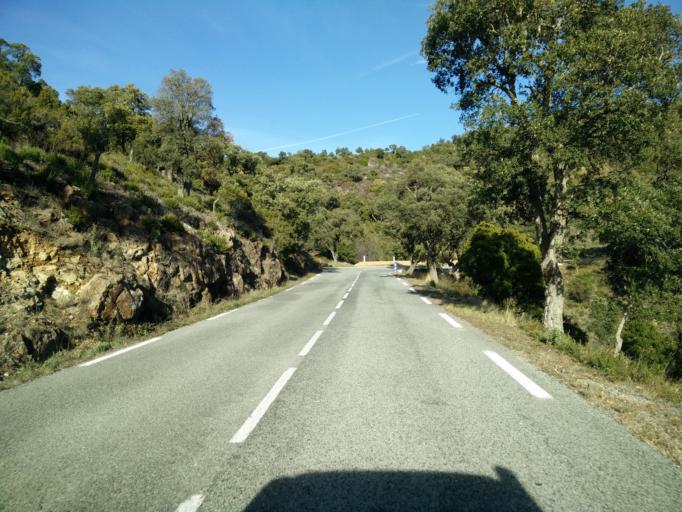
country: FR
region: Provence-Alpes-Cote d'Azur
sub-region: Departement du Var
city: Saint-Raphael
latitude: 43.5004
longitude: 6.7814
